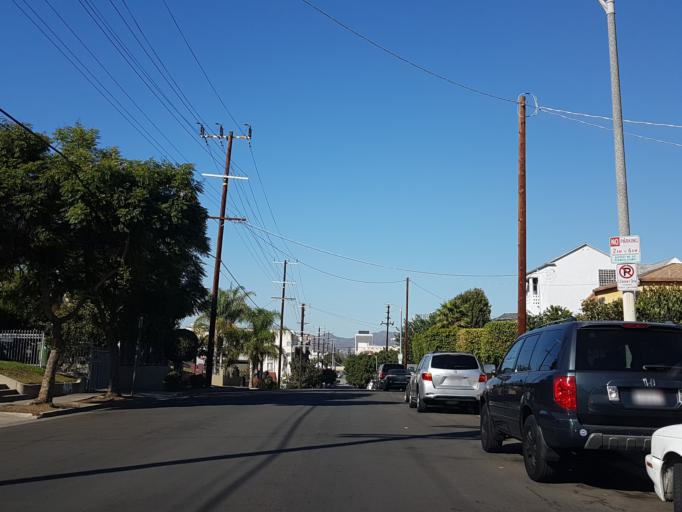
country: US
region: California
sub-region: Los Angeles County
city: Silver Lake
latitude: 34.0493
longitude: -118.3052
